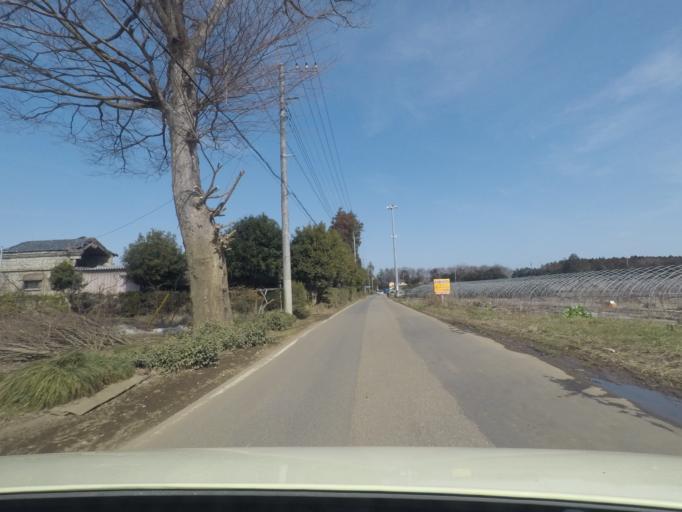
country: JP
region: Ibaraki
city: Okunoya
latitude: 36.2258
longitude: 140.4468
